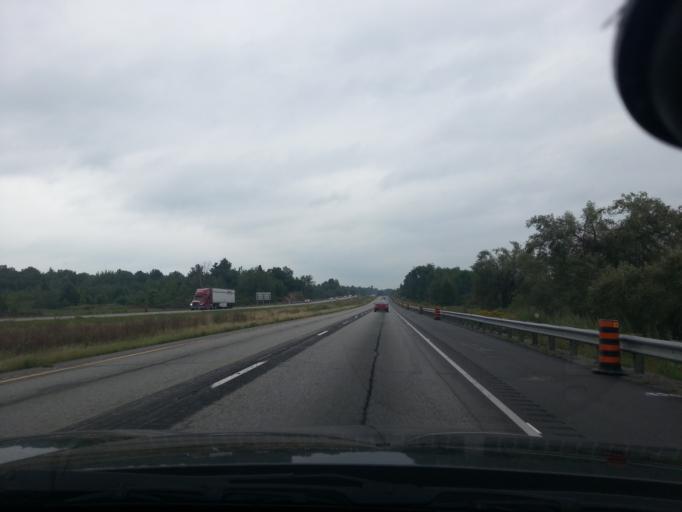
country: US
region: New York
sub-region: Jefferson County
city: Alexandria Bay
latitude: 44.3884
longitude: -75.9627
